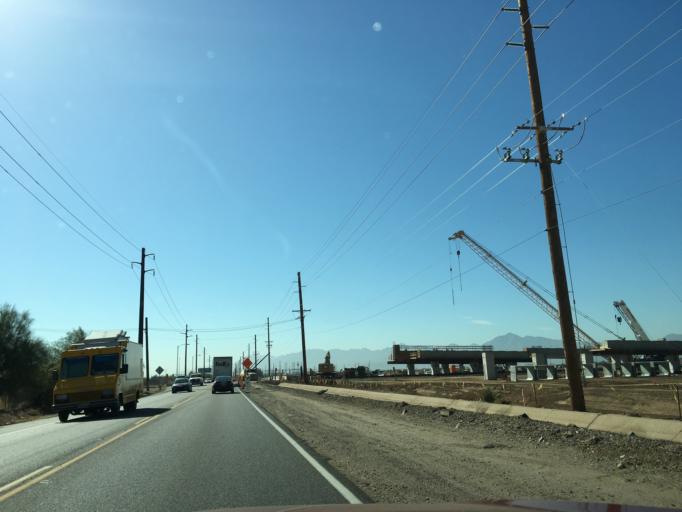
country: US
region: Arizona
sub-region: Maricopa County
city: Laveen
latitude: 33.4312
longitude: -112.1865
